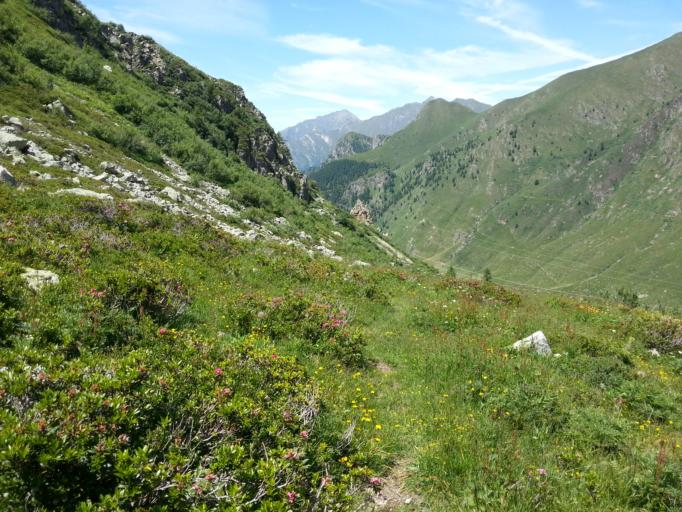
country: IT
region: Lombardy
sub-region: Provincia di Sondrio
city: Gerola Alta
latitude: 46.0257
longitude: 9.5083
